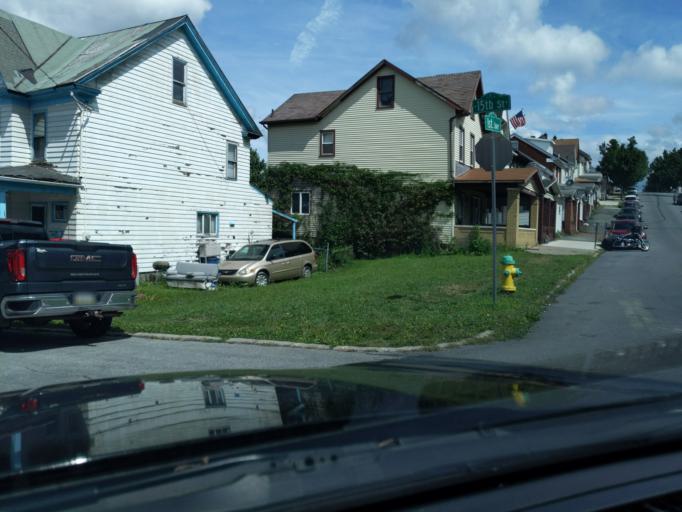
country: US
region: Pennsylvania
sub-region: Blair County
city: Altoona
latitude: 40.5072
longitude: -78.3943
